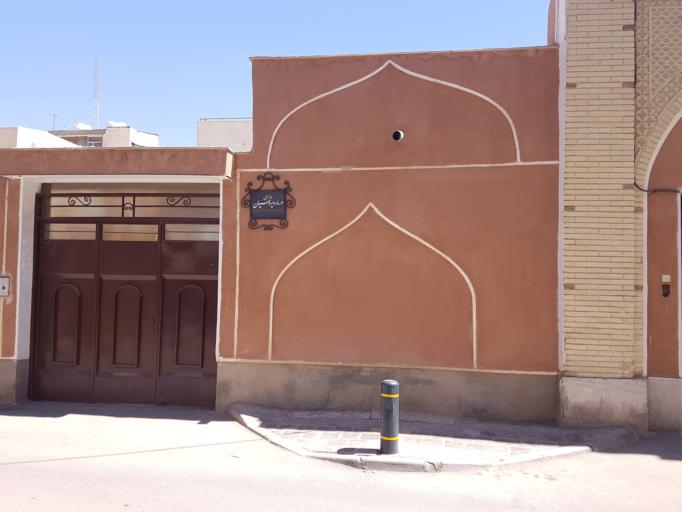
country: IR
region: Isfahan
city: Isfahan
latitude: 32.6360
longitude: 51.6533
